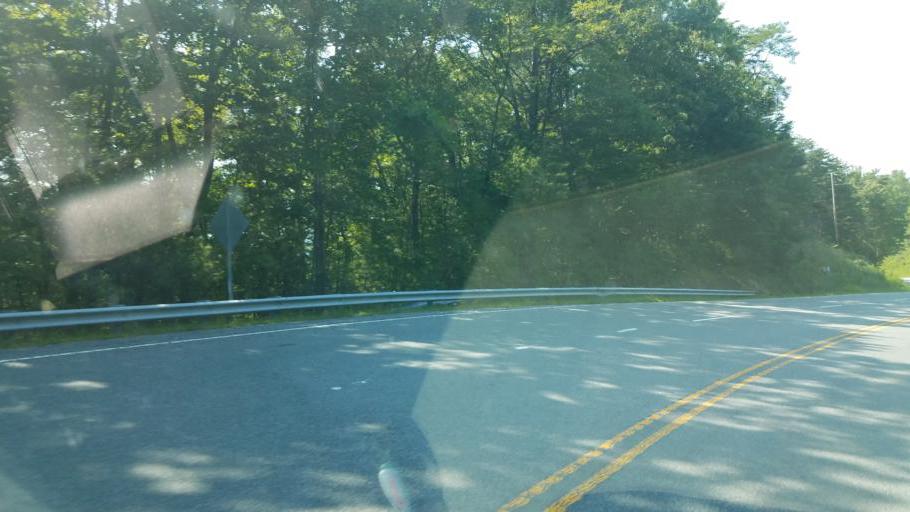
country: US
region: North Carolina
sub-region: Burke County
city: Glen Alpine
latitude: 35.9219
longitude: -81.8138
